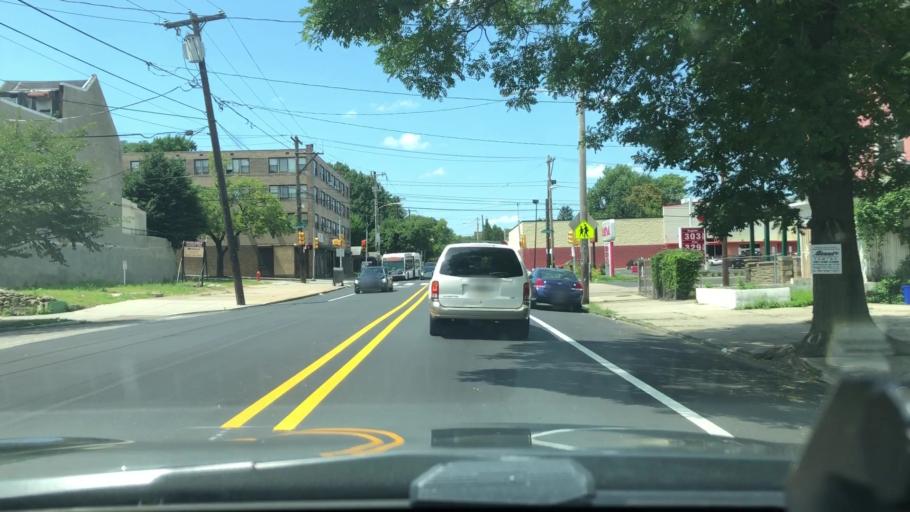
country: US
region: Pennsylvania
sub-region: Montgomery County
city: Wyndmoor
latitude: 40.0502
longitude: -75.1725
